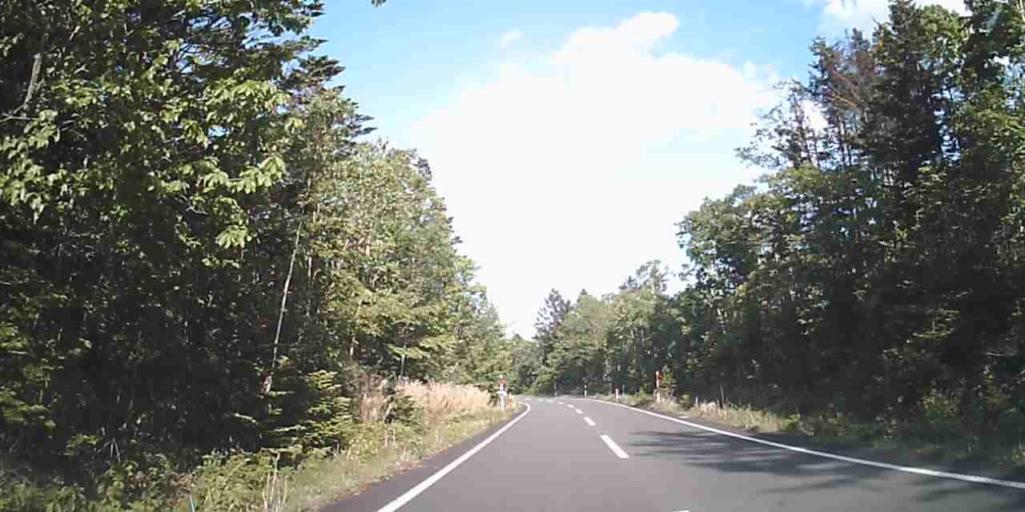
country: JP
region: Hokkaido
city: Shiraoi
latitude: 42.6886
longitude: 141.4302
